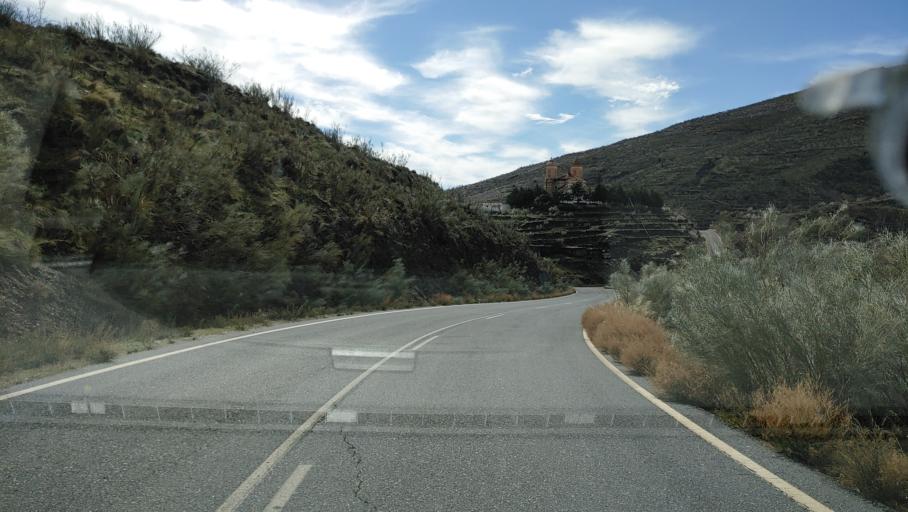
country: ES
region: Andalusia
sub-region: Provincia de Almeria
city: Ohanes
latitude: 37.0654
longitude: -2.7309
